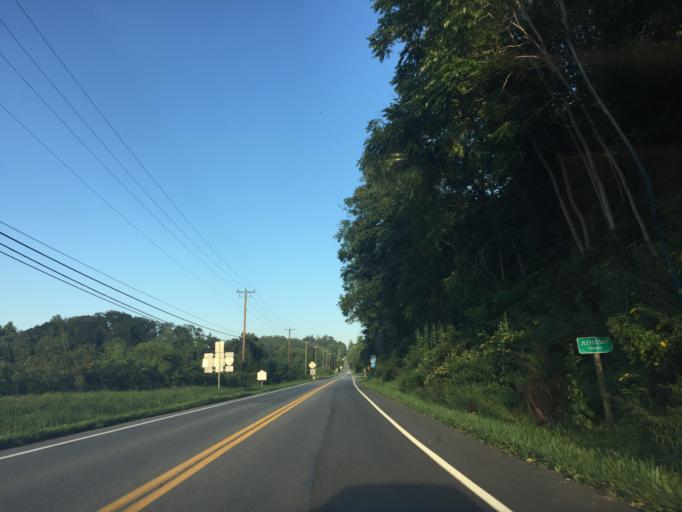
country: US
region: Virginia
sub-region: Albemarle County
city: Crozet
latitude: 38.0619
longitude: -78.6463
